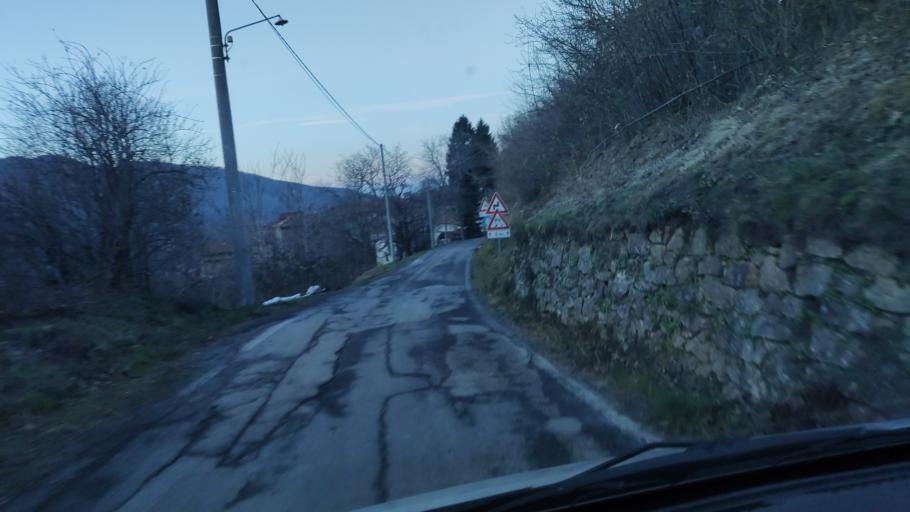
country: IT
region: Piedmont
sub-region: Provincia di Cuneo
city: Viola
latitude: 44.2879
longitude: 7.9837
